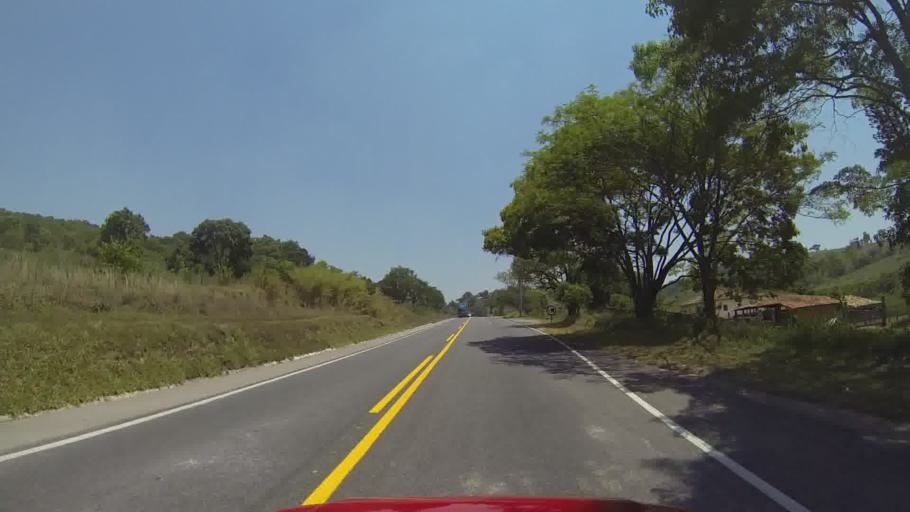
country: BR
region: Minas Gerais
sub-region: Itapecerica
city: Itapecerica
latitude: -20.2944
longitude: -45.1667
